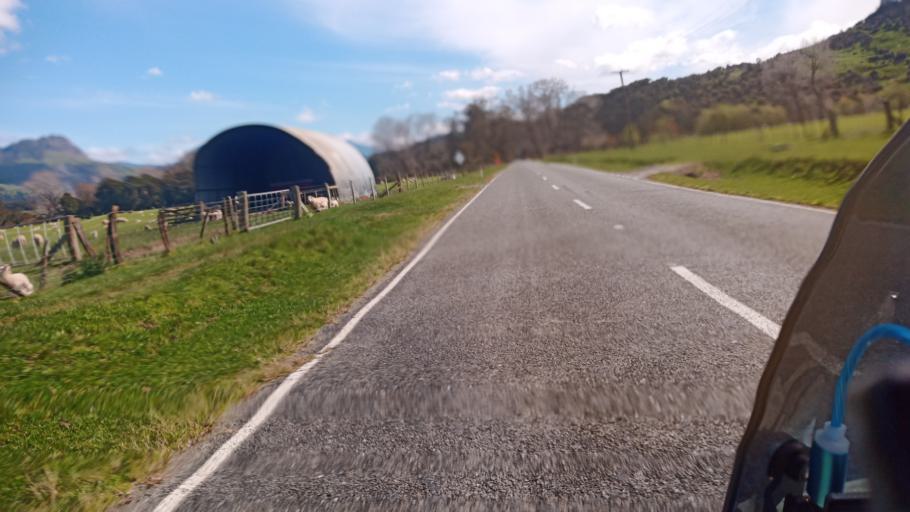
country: NZ
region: Gisborne
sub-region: Gisborne District
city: Gisborne
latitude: -37.8651
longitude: 178.2557
